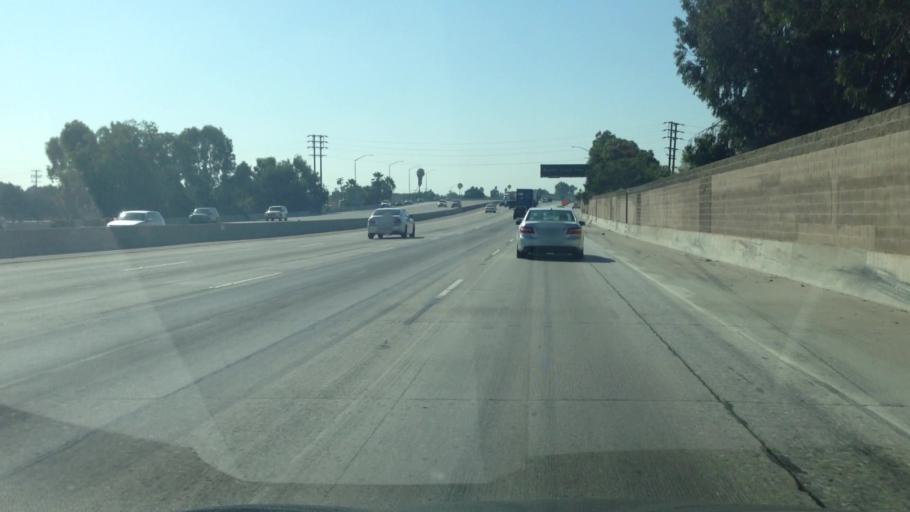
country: US
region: California
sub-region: Los Angeles County
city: West Carson
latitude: 33.7950
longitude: -118.2848
